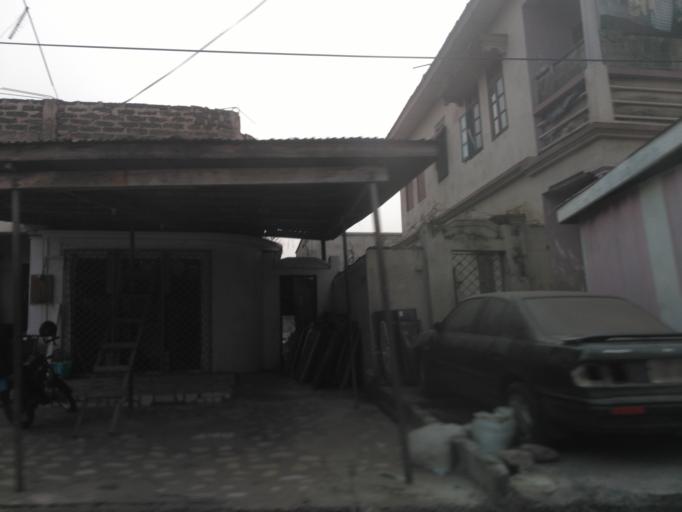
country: GH
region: Ashanti
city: Tafo
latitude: 6.7113
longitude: -1.6158
